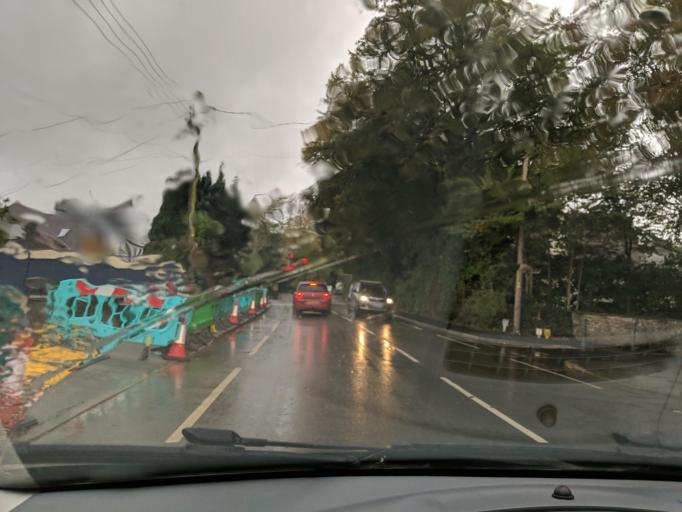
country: GB
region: England
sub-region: Cornwall
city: Wadebridge
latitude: 50.5210
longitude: -4.8298
